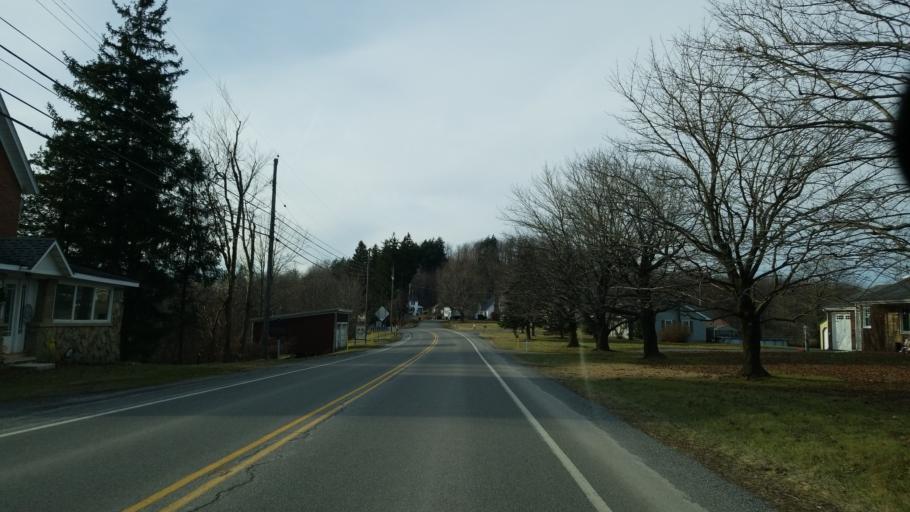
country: US
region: Pennsylvania
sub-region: Clearfield County
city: Sandy
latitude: 41.0513
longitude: -78.7083
